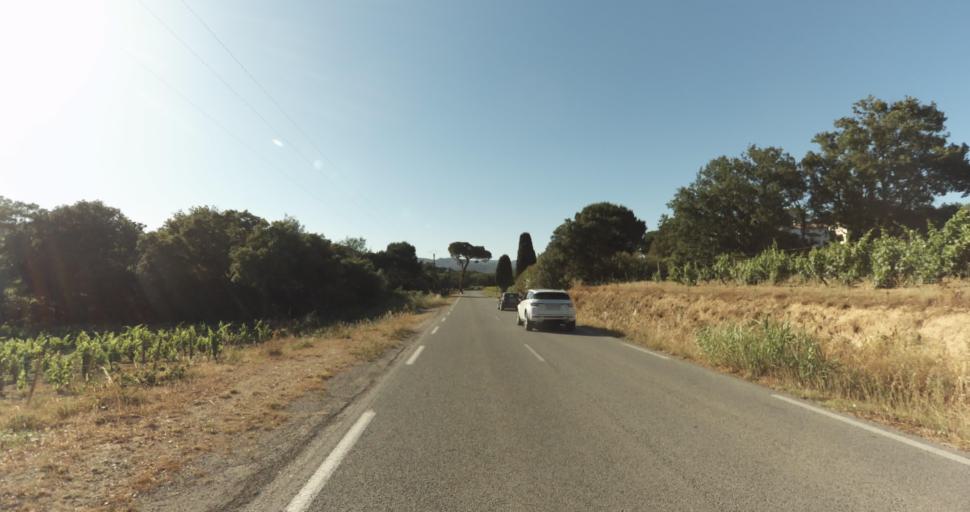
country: FR
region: Provence-Alpes-Cote d'Azur
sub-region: Departement du Var
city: Gassin
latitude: 43.2423
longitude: 6.5969
